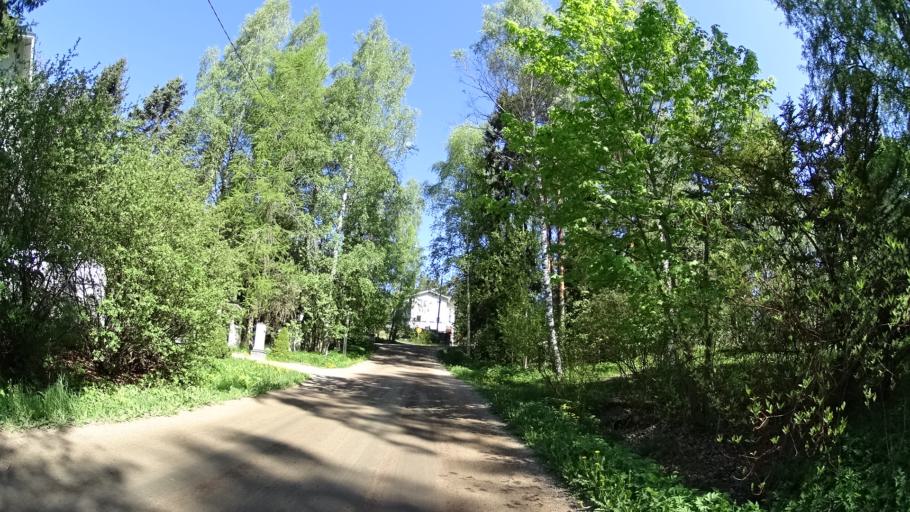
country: FI
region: Uusimaa
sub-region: Helsinki
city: Espoo
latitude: 60.1605
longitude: 24.6178
